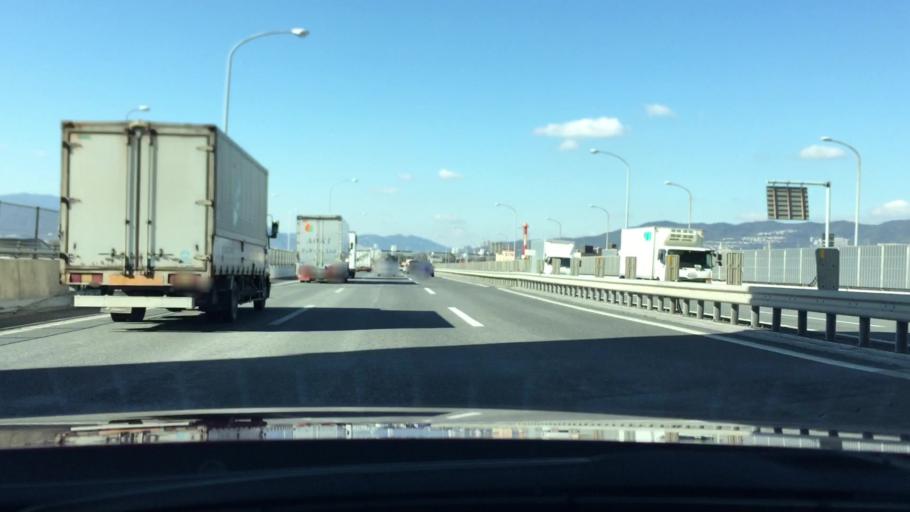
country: JP
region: Hyogo
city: Kawanishi
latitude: 34.8104
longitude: 135.4207
